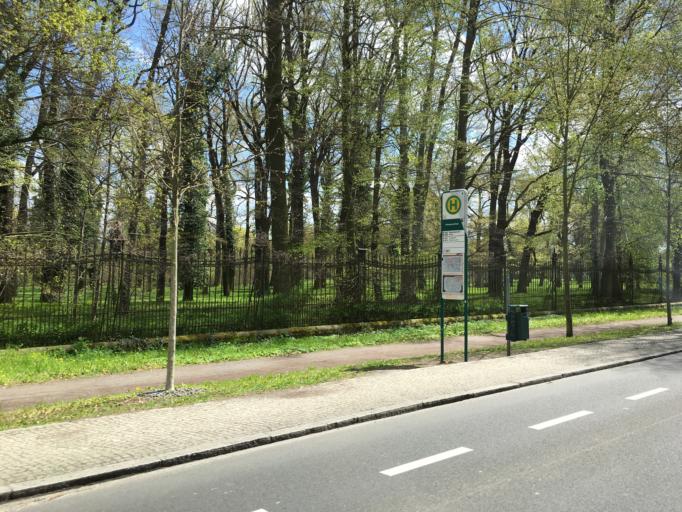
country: DE
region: Brandenburg
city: Potsdam
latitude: 52.4052
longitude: 13.0140
